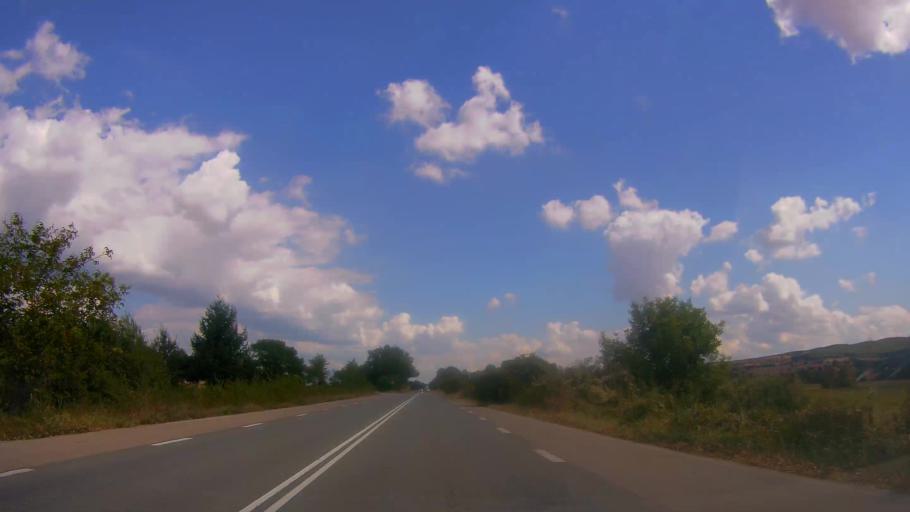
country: BG
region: Sliven
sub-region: Obshtina Tvurditsa
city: Tvurditsa
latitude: 42.6566
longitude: 25.8968
